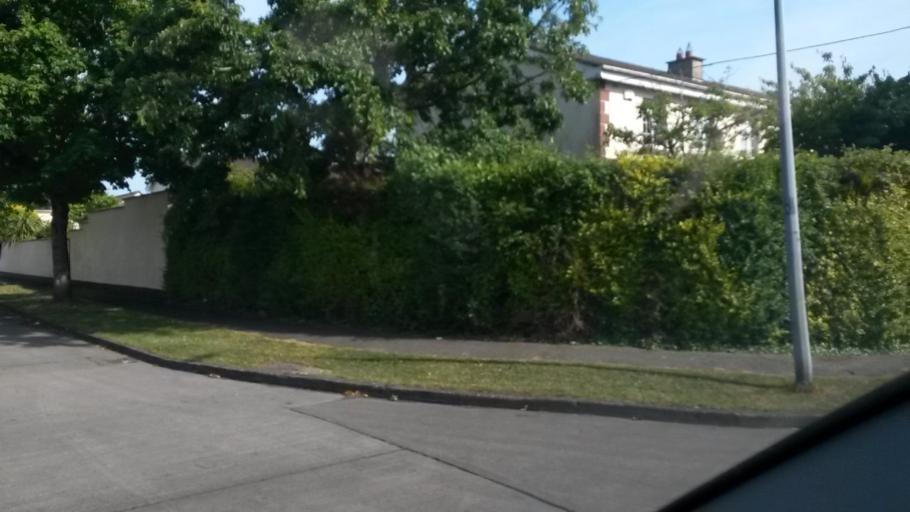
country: IE
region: Leinster
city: Lusk
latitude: 53.5239
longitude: -6.1610
